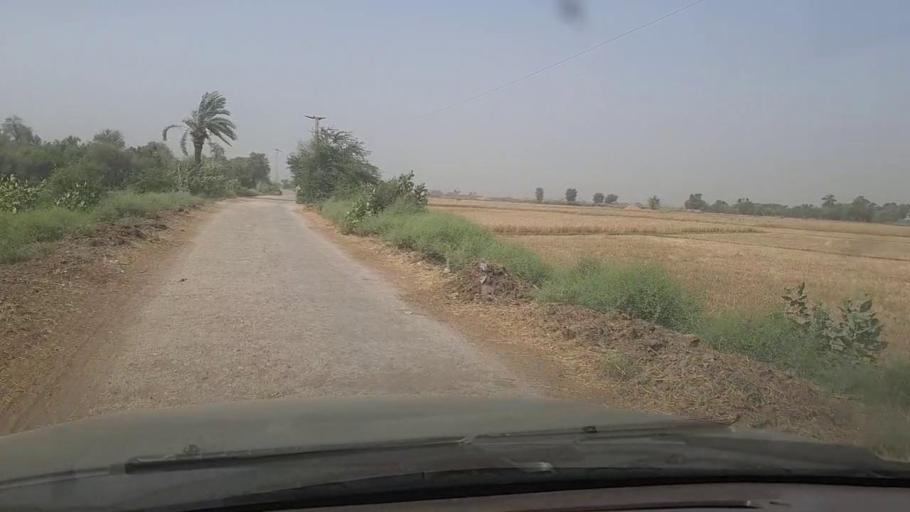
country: PK
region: Sindh
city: Garhi Yasin
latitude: 27.8606
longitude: 68.5486
